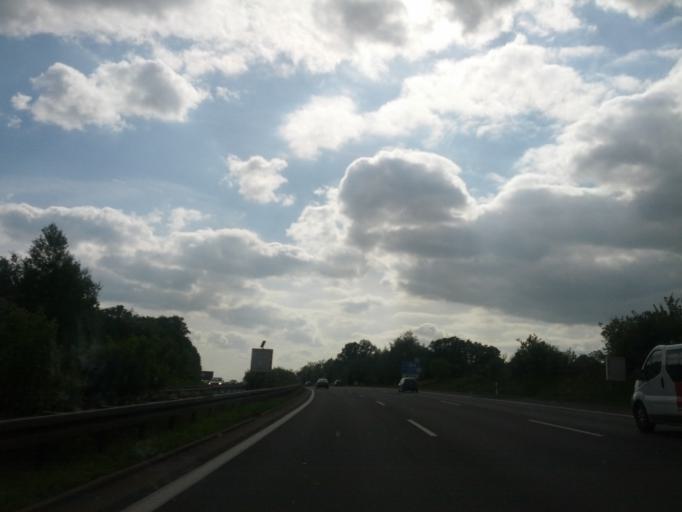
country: DE
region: Saxony
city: Nossen
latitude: 51.0480
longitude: 13.3425
